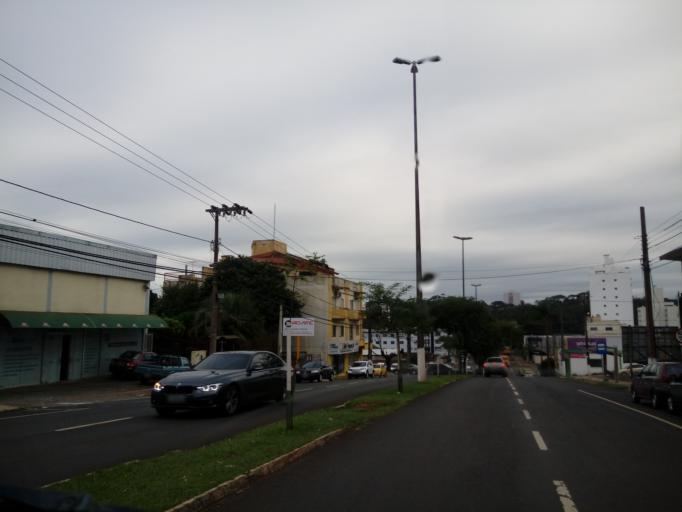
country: BR
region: Santa Catarina
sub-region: Chapeco
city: Chapeco
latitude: -27.0913
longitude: -52.6159
